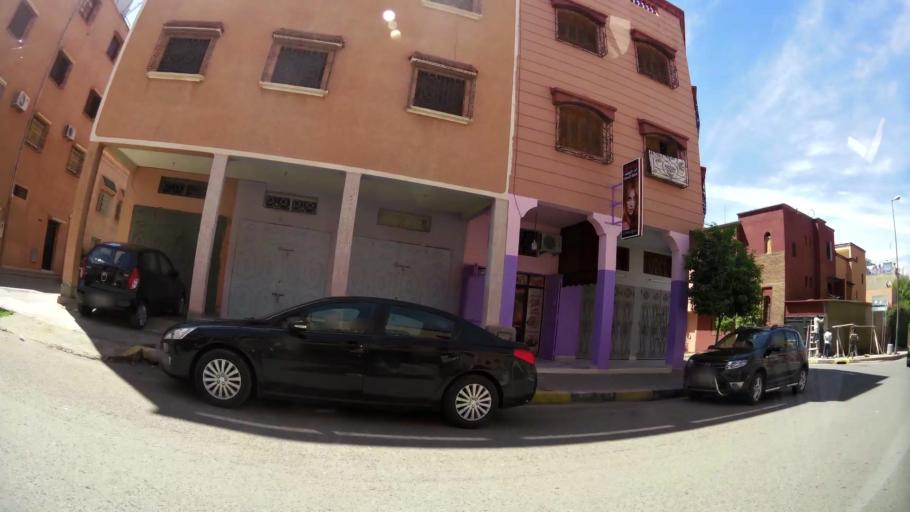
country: MA
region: Marrakech-Tensift-Al Haouz
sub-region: Marrakech
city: Marrakesh
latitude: 31.6449
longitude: -8.0633
